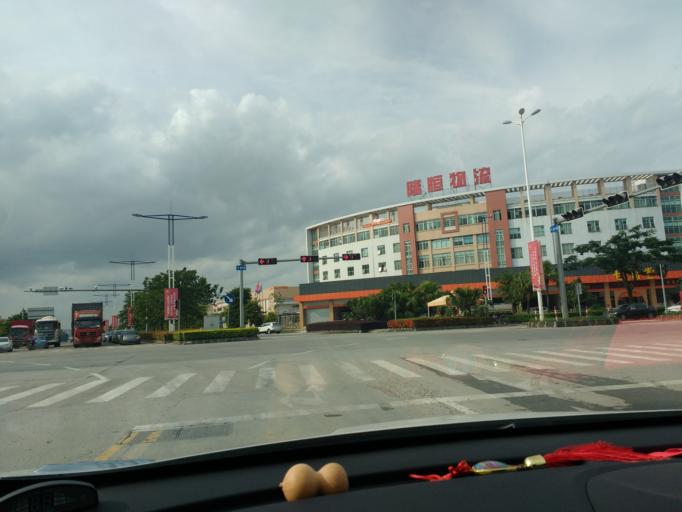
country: CN
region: Guangdong
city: Xinhui
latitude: 22.4559
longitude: 113.0564
